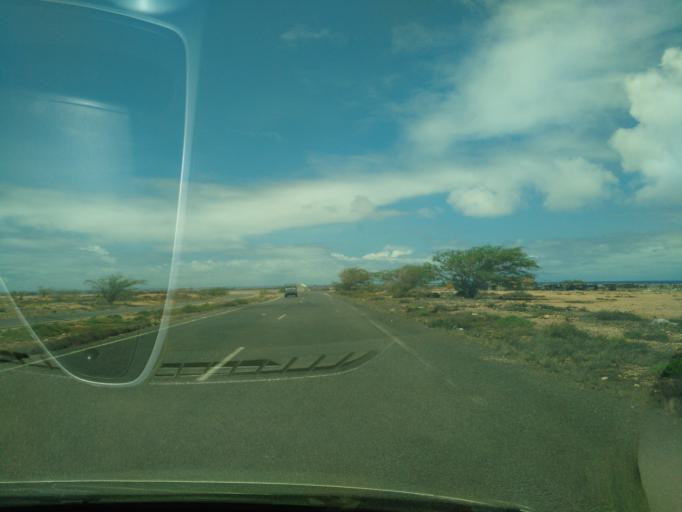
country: CV
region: Sal
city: Santa Maria
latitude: 16.6358
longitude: -22.9173
